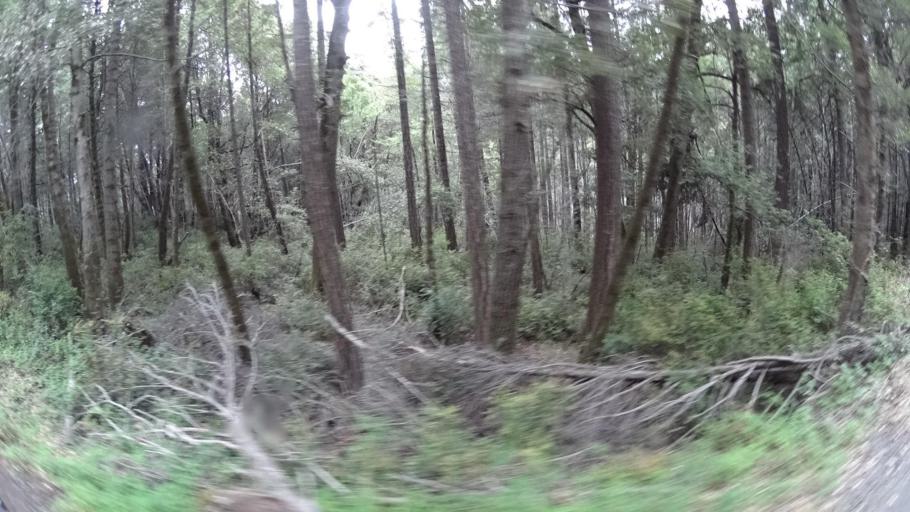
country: US
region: California
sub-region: Humboldt County
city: Willow Creek
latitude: 41.2019
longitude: -123.7617
